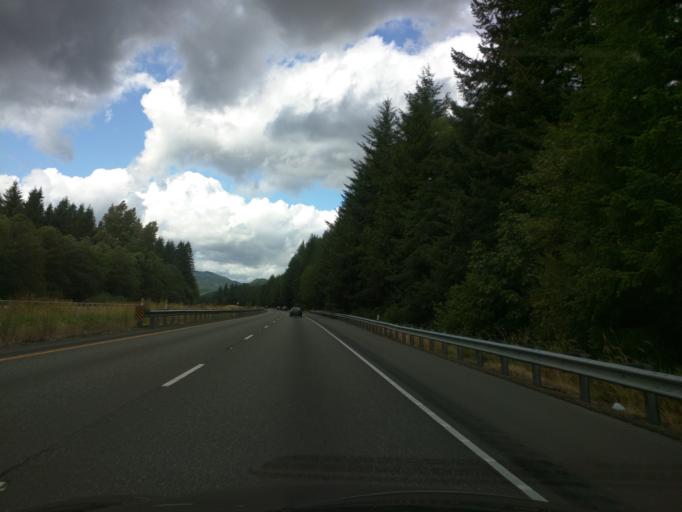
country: US
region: Washington
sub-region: Skagit County
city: Burlington
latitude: 48.5904
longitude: -122.3440
